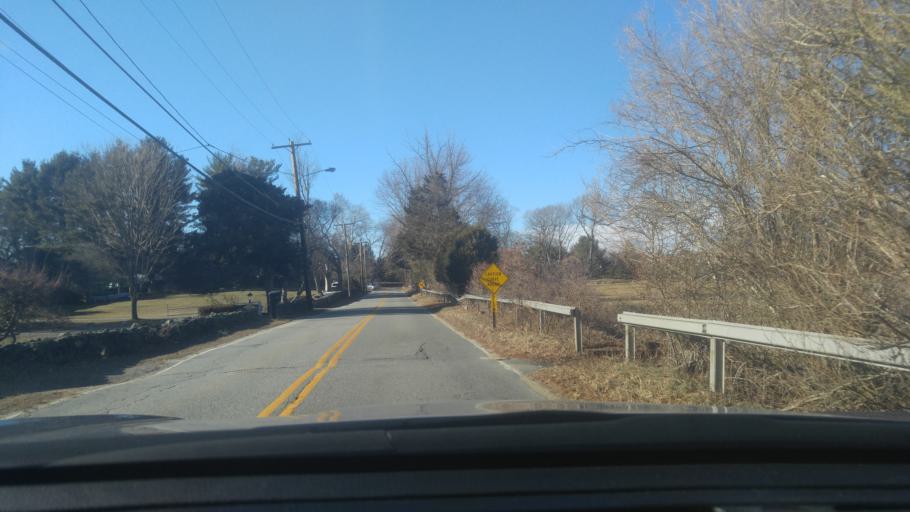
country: US
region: Rhode Island
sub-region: Kent County
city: East Greenwich
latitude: 41.6396
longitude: -71.4190
